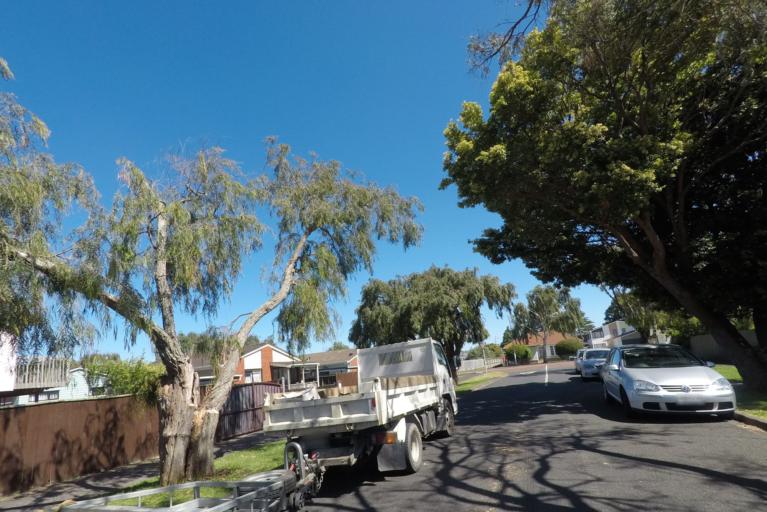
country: NZ
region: Auckland
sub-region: Auckland
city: Rosebank
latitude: -36.8892
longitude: 174.6819
